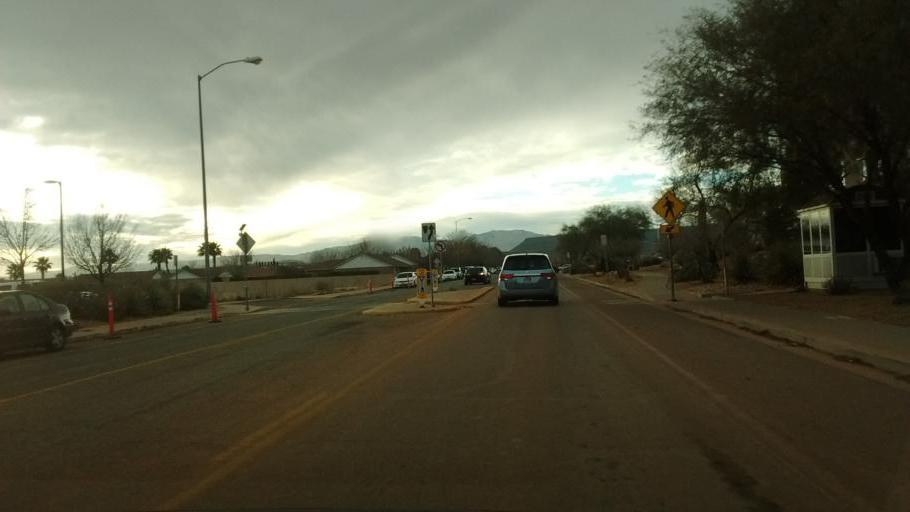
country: US
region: Utah
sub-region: Washington County
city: Saint George
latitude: 37.0963
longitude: -113.5532
